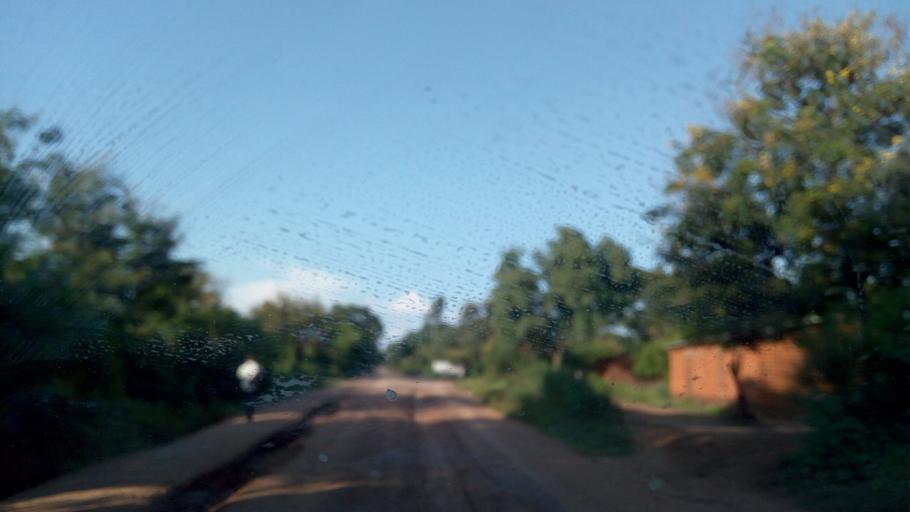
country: BI
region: Bururi
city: Rumonge
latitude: -4.1873
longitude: 29.0537
